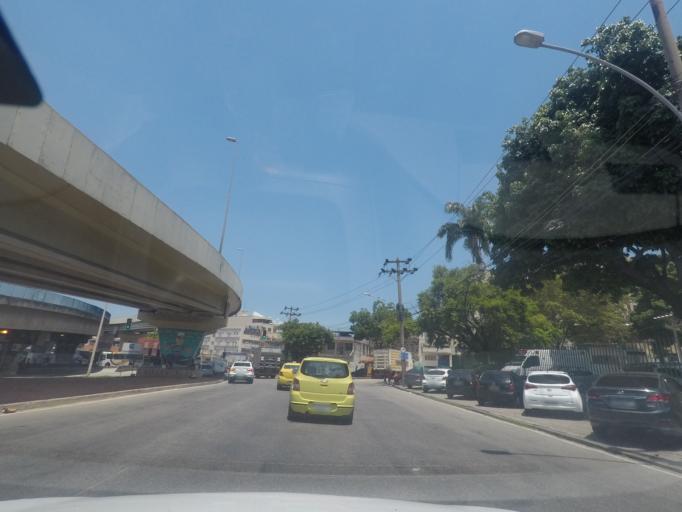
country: BR
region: Rio de Janeiro
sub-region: Duque De Caxias
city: Duque de Caxias
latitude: -22.8381
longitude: -43.2860
